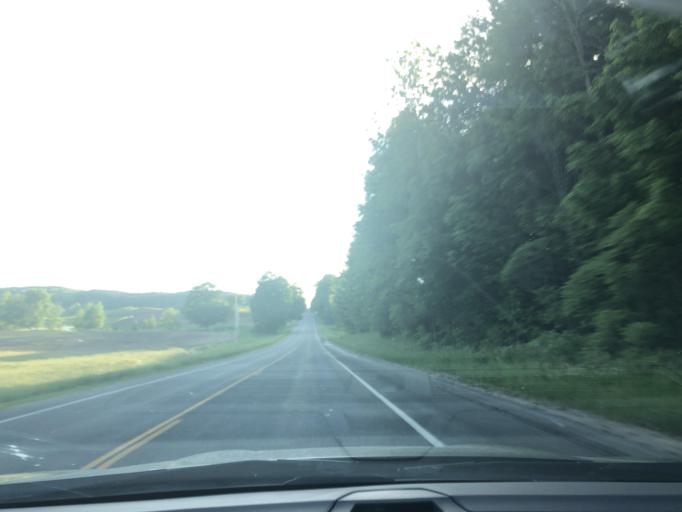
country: US
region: Michigan
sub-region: Missaukee County
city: Lake City
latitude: 44.4667
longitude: -85.0955
